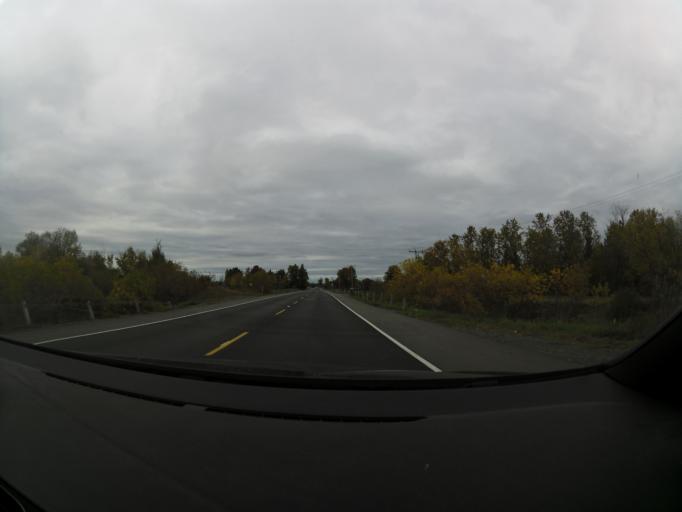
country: CA
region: Ontario
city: Bells Corners
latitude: 45.4015
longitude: -75.9952
